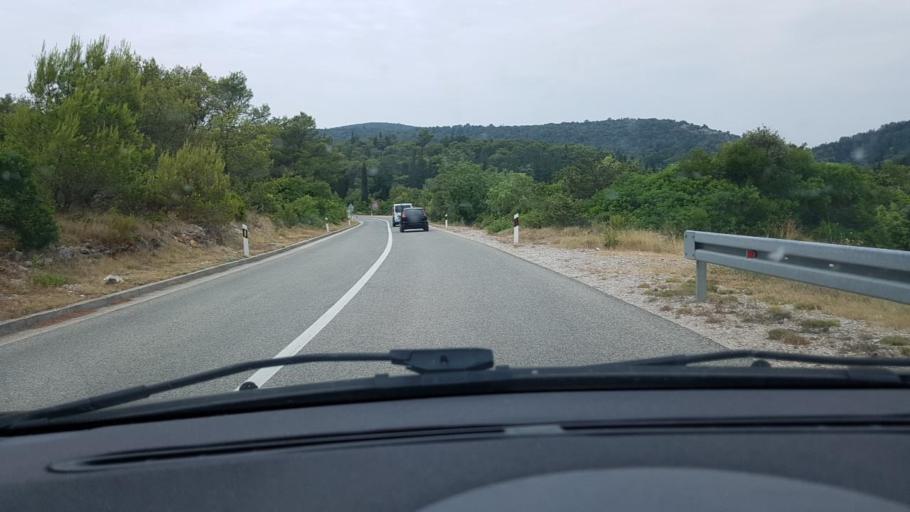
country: HR
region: Dubrovacko-Neretvanska
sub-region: Grad Korcula
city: Zrnovo
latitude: 42.9469
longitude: 17.0438
